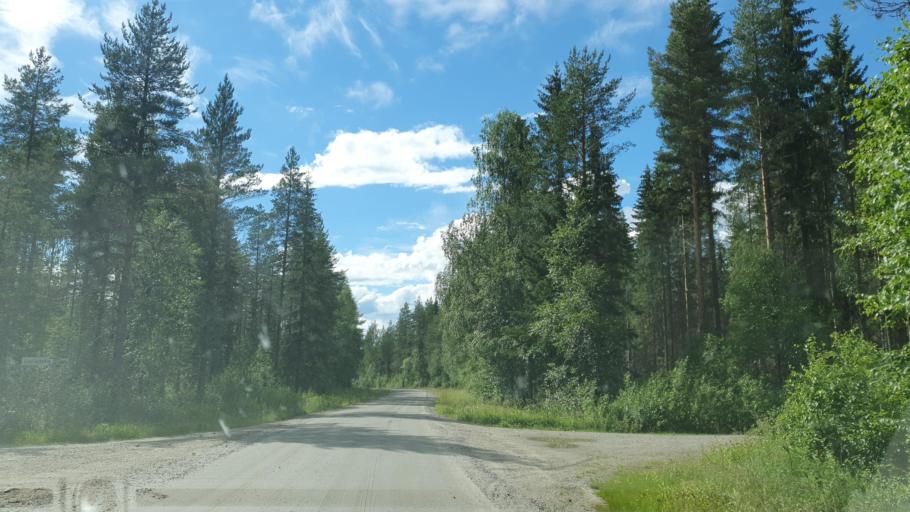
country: FI
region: Kainuu
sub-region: Kehys-Kainuu
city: Kuhmo
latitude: 64.1624
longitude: 29.8458
